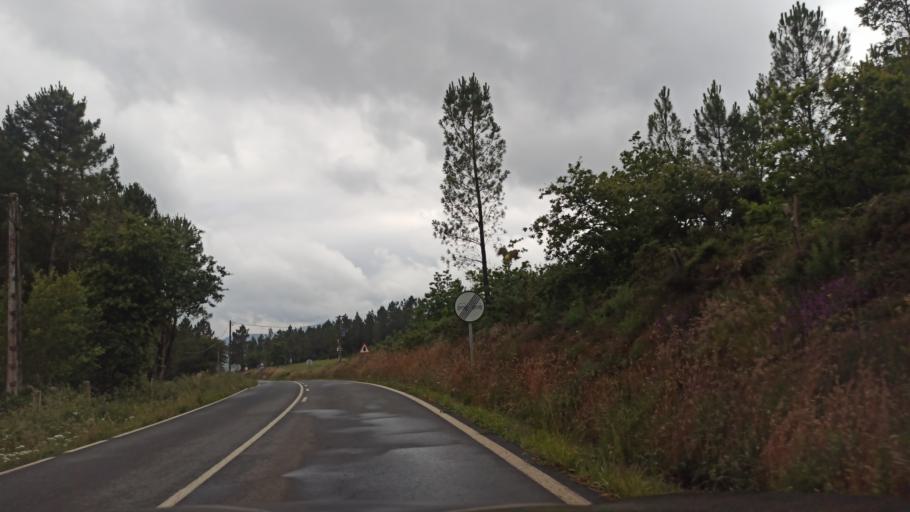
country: ES
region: Galicia
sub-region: Provincia da Coruna
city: Santiso
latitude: 42.7783
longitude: -8.0798
